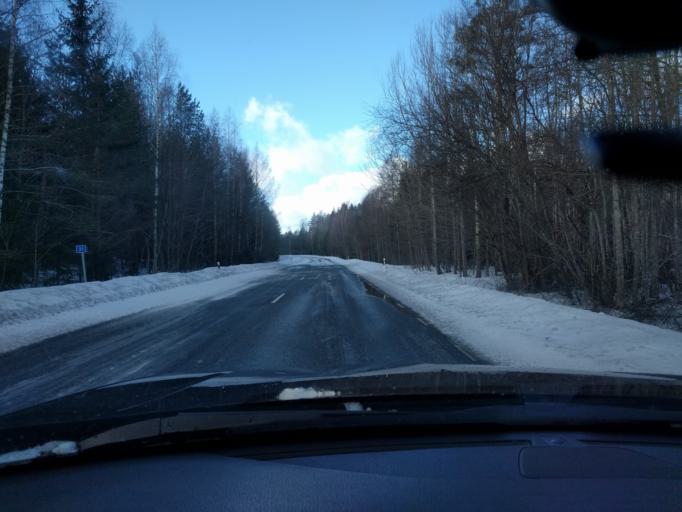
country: EE
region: Harju
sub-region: Anija vald
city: Kehra
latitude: 59.2183
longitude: 25.4775
